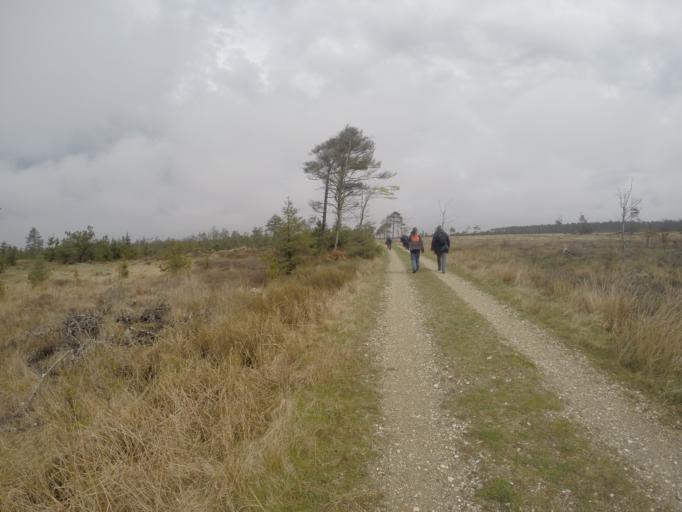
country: DK
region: North Denmark
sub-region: Thisted Kommune
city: Hanstholm
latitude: 57.0398
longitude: 8.5580
